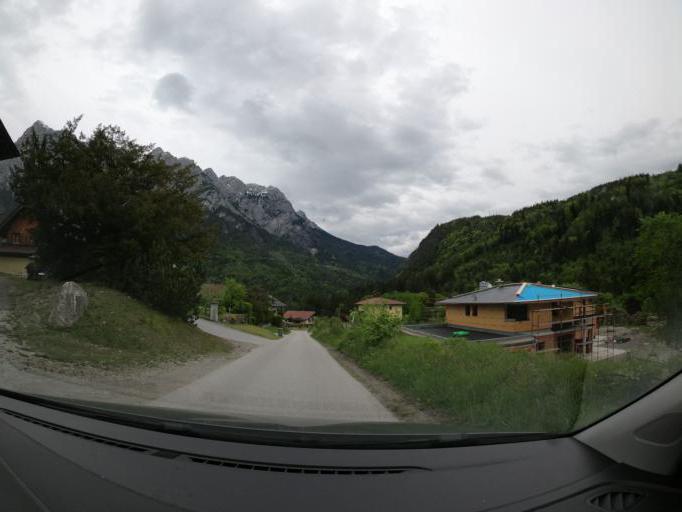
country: AT
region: Salzburg
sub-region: Politischer Bezirk Sankt Johann im Pongau
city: Werfen
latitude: 47.4906
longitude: 13.1652
